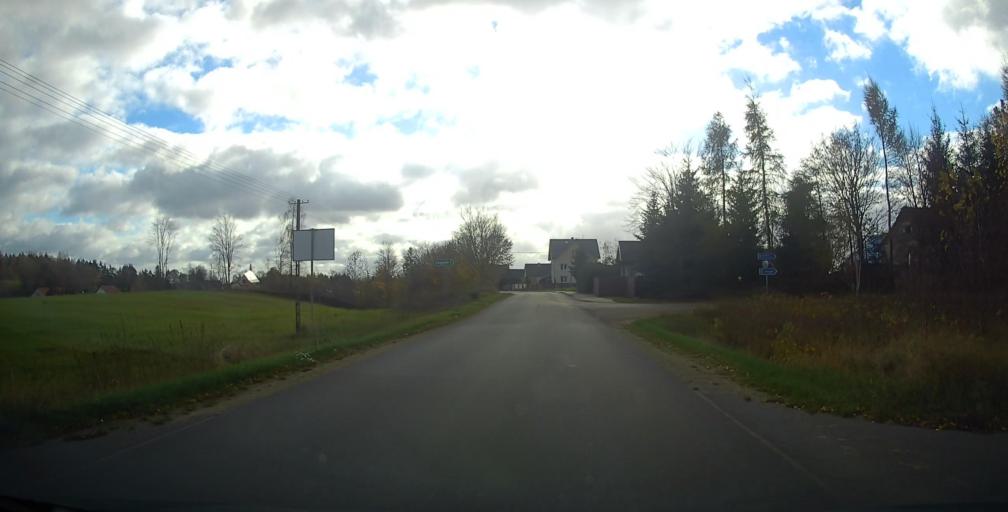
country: PL
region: Podlasie
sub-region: Suwalki
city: Suwalki
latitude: 54.2919
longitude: 22.8789
